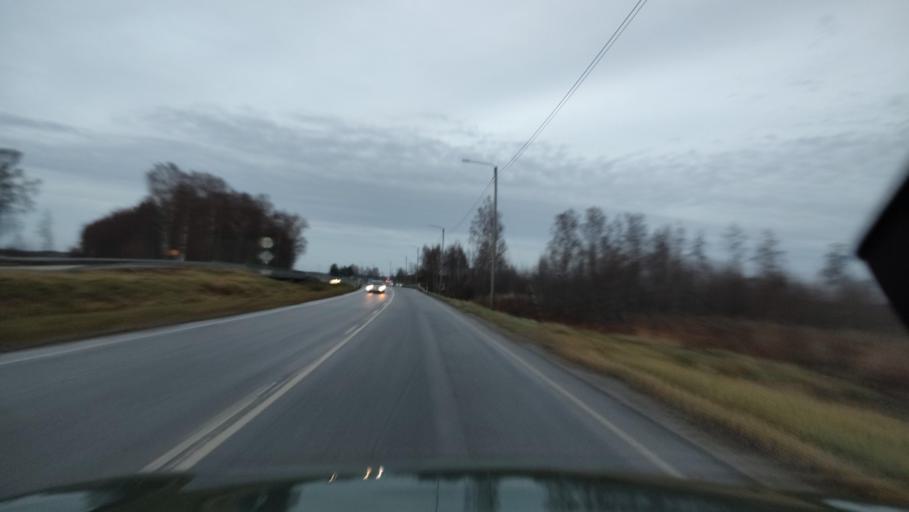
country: FI
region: Ostrobothnia
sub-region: Vaasa
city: Ristinummi
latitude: 63.0412
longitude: 21.7397
